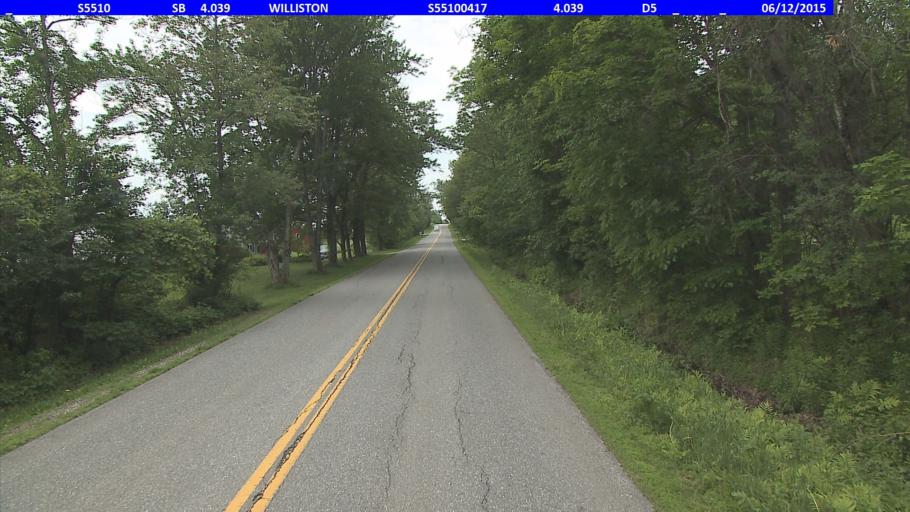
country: US
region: Vermont
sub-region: Chittenden County
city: Williston
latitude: 44.4272
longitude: -73.0761
